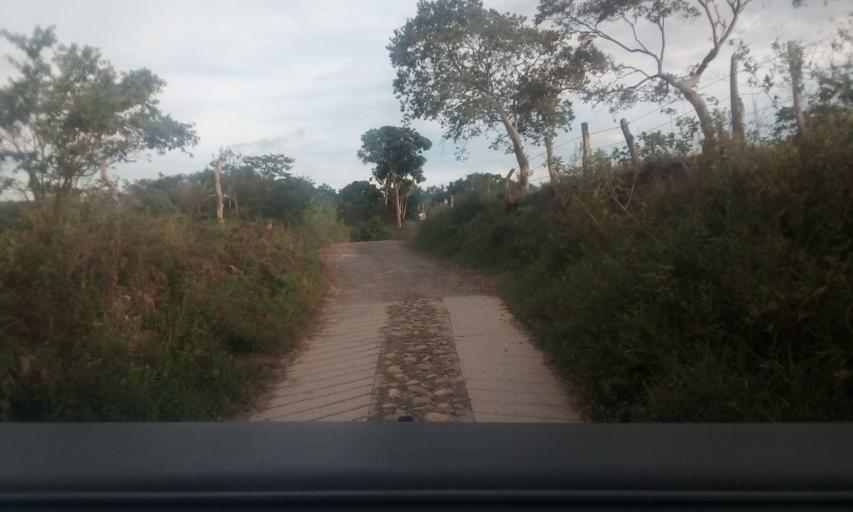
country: CO
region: Boyaca
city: Santana
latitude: 6.0191
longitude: -73.5126
